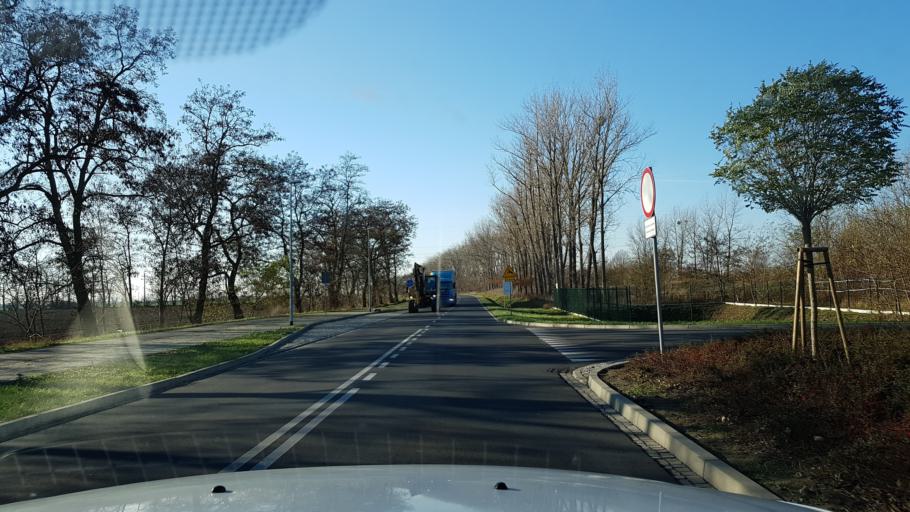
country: PL
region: West Pomeranian Voivodeship
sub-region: Powiat stargardzki
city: Stargard Szczecinski
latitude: 53.3257
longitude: 15.0068
